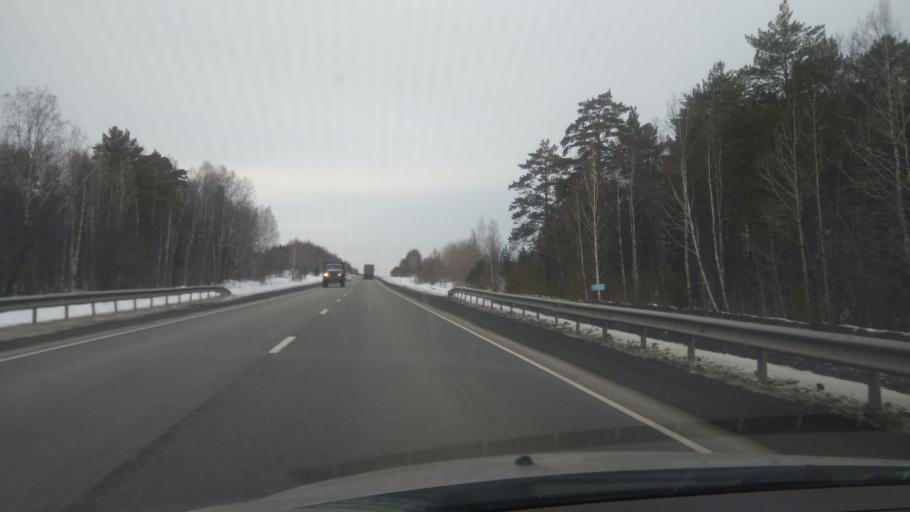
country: RU
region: Sverdlovsk
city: Bisert'
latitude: 56.8205
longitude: 58.7579
